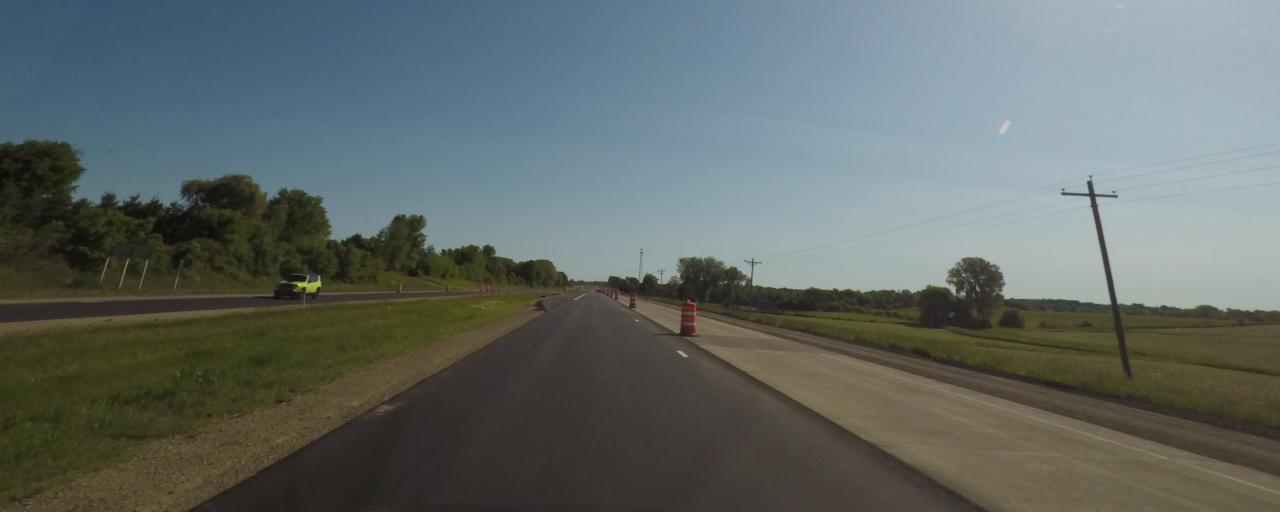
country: US
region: Wisconsin
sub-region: Columbia County
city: Columbus
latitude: 43.3981
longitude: -88.9303
